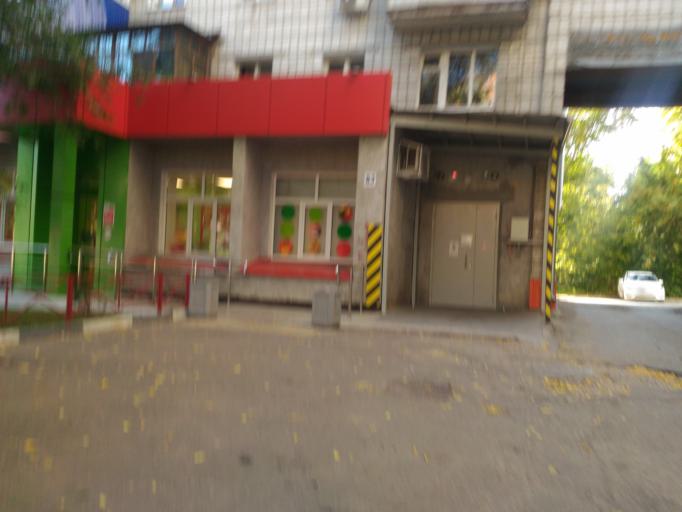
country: RU
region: Ulyanovsk
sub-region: Ulyanovskiy Rayon
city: Ulyanovsk
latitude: 54.3023
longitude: 48.3787
